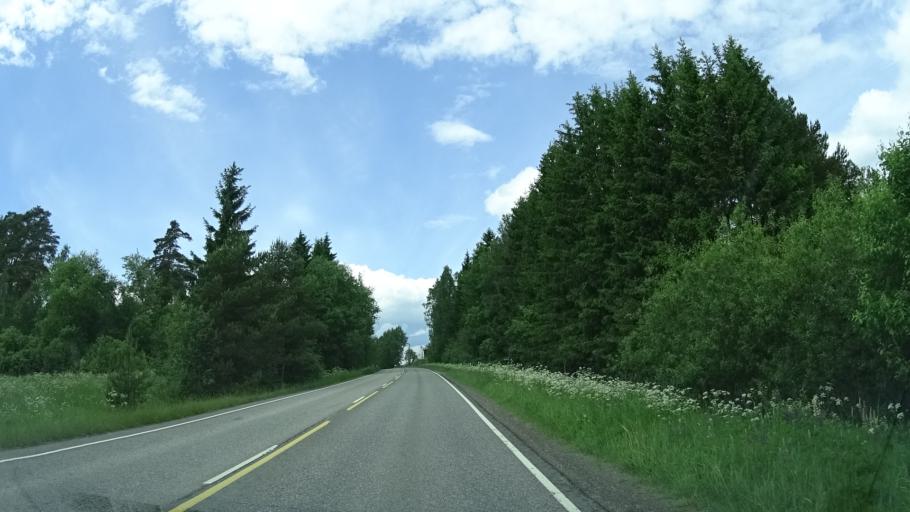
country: FI
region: Uusimaa
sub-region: Helsinki
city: Espoo
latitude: 60.1979
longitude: 24.5574
